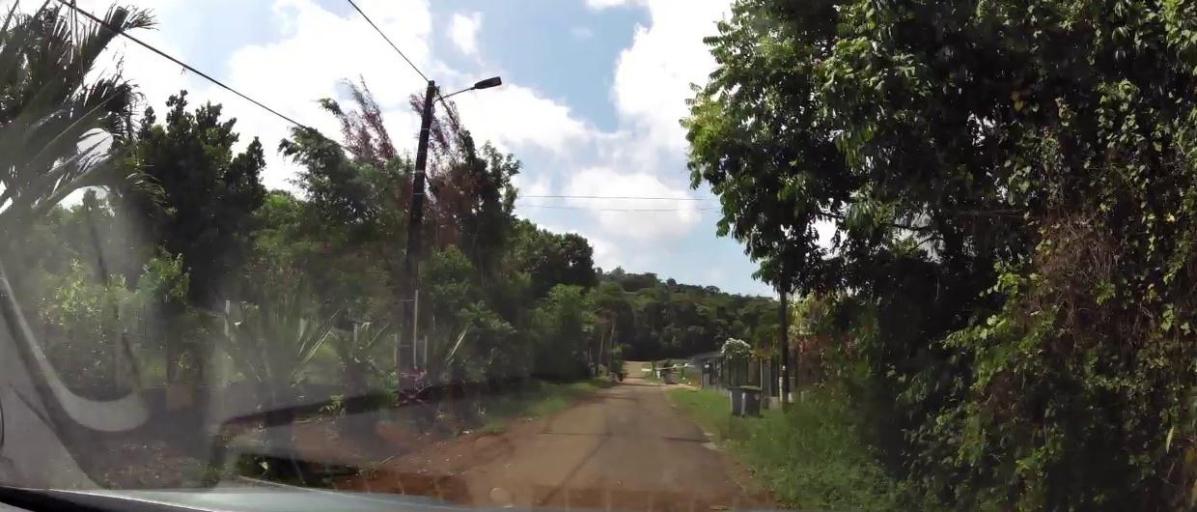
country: GF
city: Macouria
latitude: 4.8791
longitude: -52.3595
